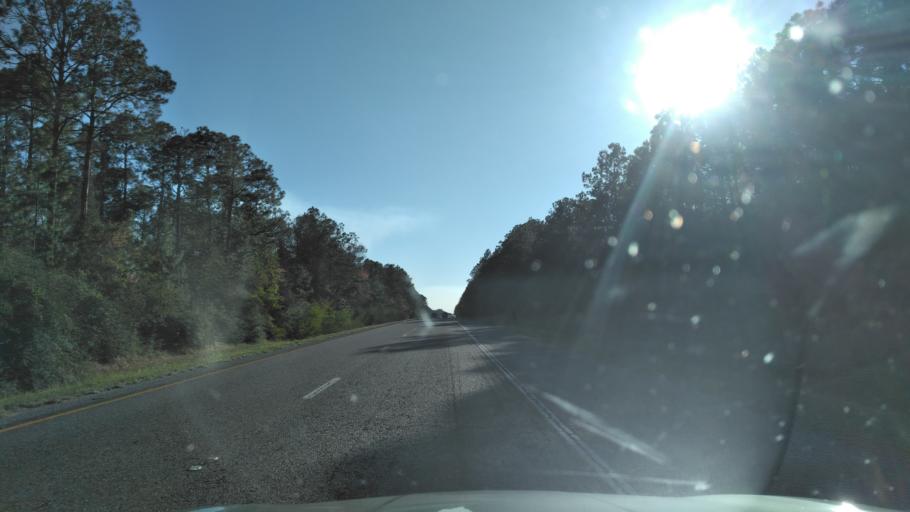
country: US
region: Alabama
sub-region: Baldwin County
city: Bay Minette
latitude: 31.0057
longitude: -87.6778
